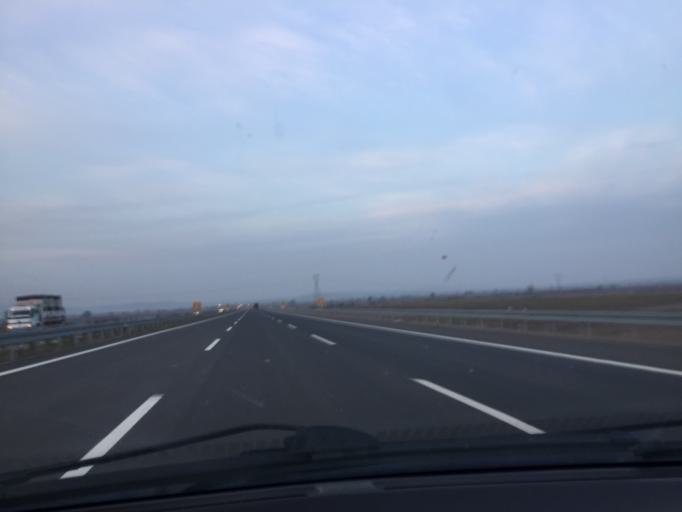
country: TR
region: Manisa
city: Halitpasa
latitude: 38.7133
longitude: 27.6485
